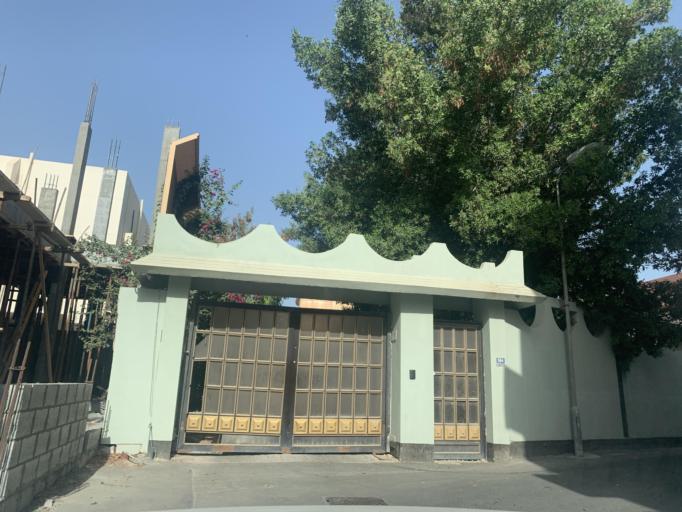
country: BH
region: Manama
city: Jidd Hafs
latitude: 26.2124
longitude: 50.5644
